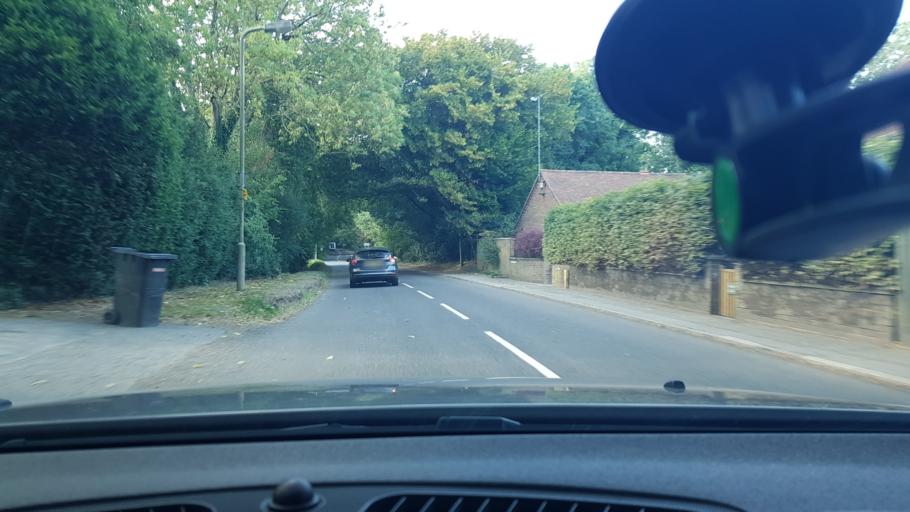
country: GB
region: England
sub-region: West Berkshire
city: Lambourn
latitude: 51.5114
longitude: -1.5354
